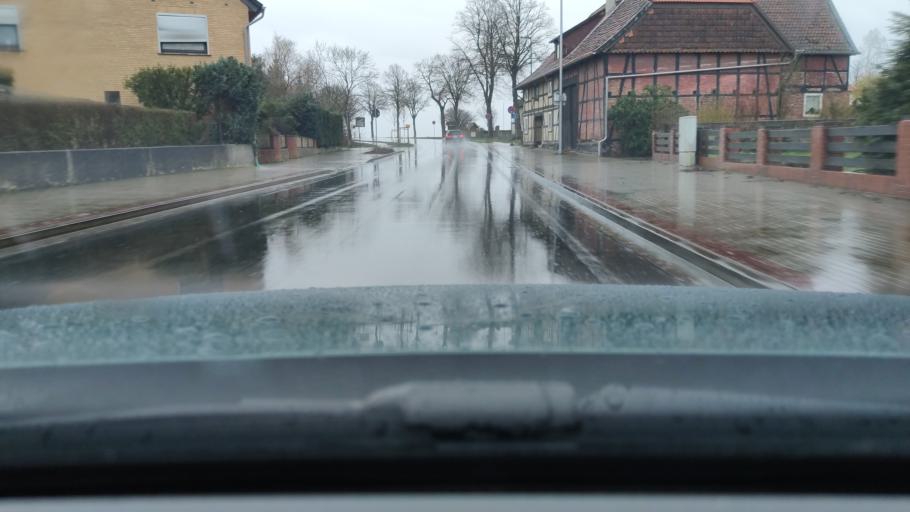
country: DE
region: Lower Saxony
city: Ilsede
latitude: 52.2835
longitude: 10.2285
